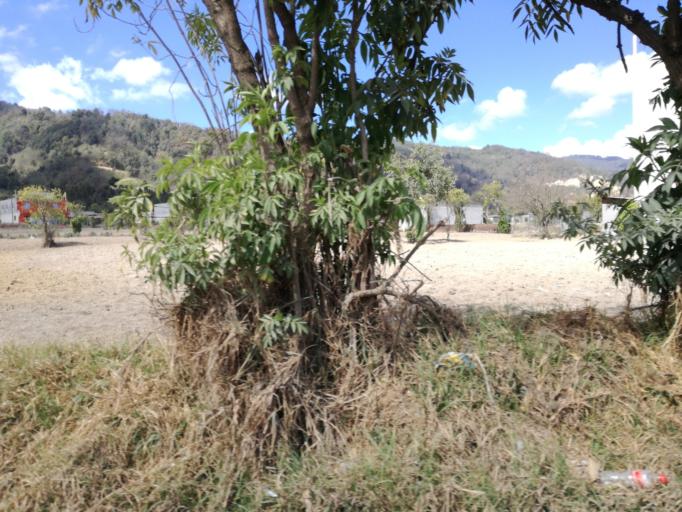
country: GT
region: Quetzaltenango
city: Almolonga
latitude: 14.7861
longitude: -91.5385
